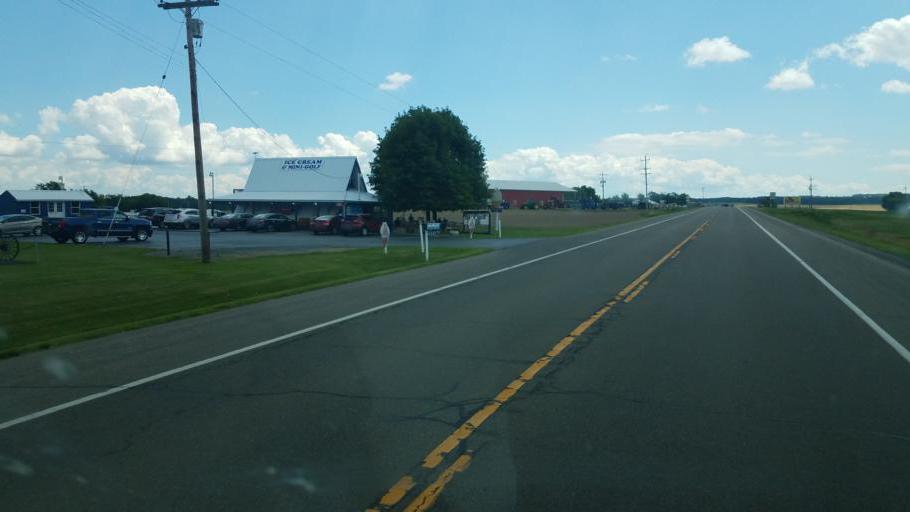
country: US
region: New York
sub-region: Yates County
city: Penn Yan
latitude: 42.6394
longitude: -77.0439
